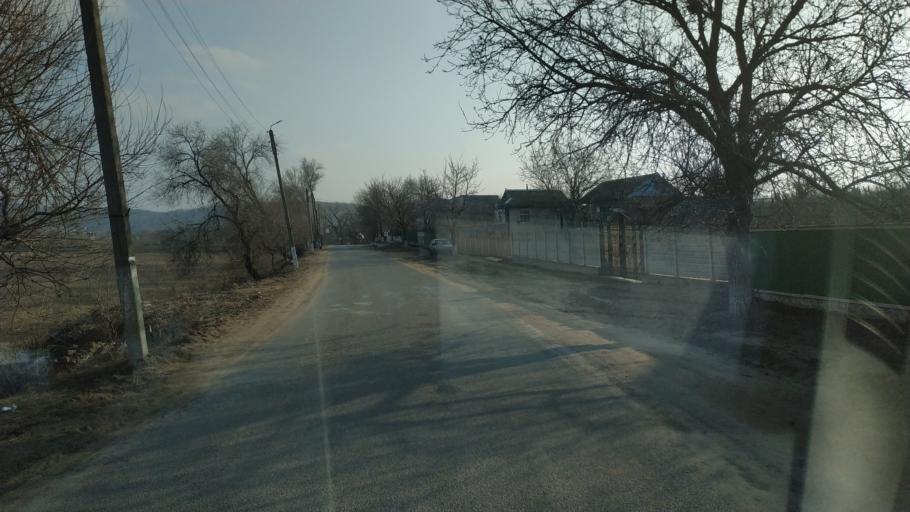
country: MD
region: Hincesti
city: Dancu
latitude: 46.7672
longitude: 28.3456
